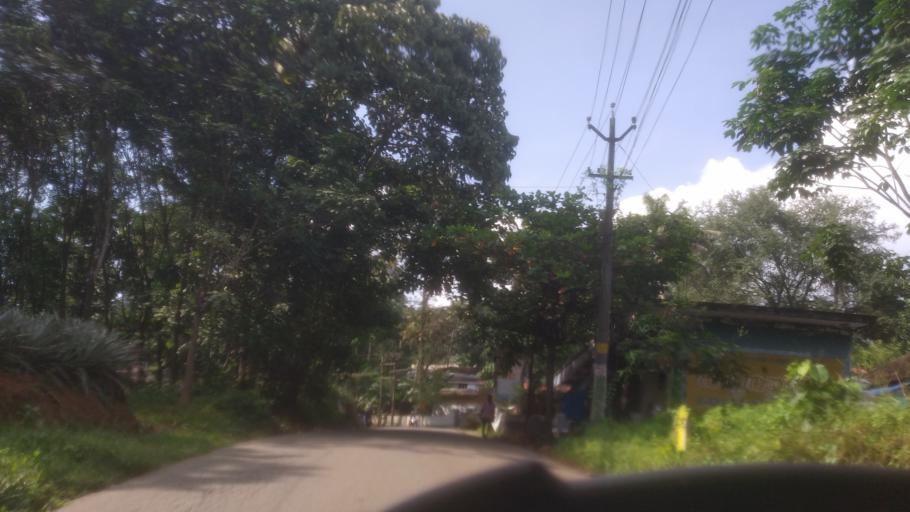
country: IN
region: Kerala
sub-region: Ernakulam
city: Muvattupula
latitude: 9.9990
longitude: 76.6354
